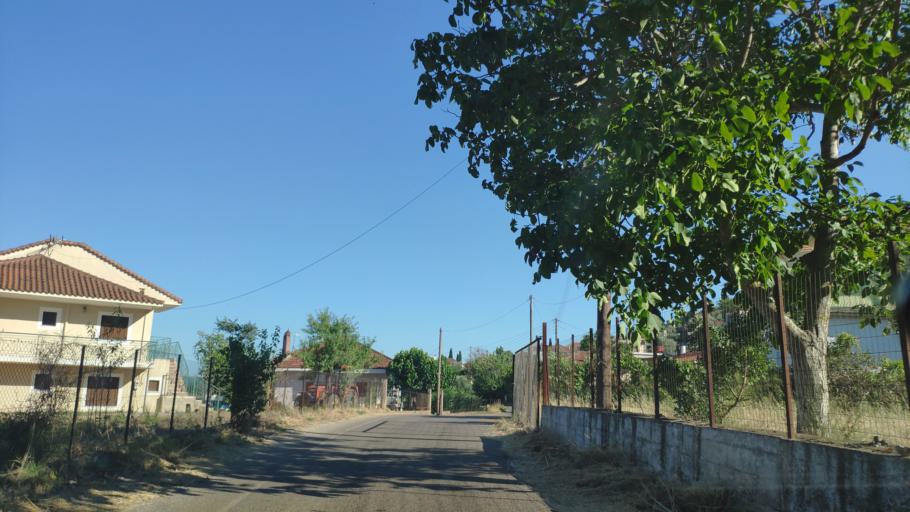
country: GR
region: West Greece
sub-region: Nomos Aitolias kai Akarnanias
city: Fitiai
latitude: 38.6638
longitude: 21.1445
